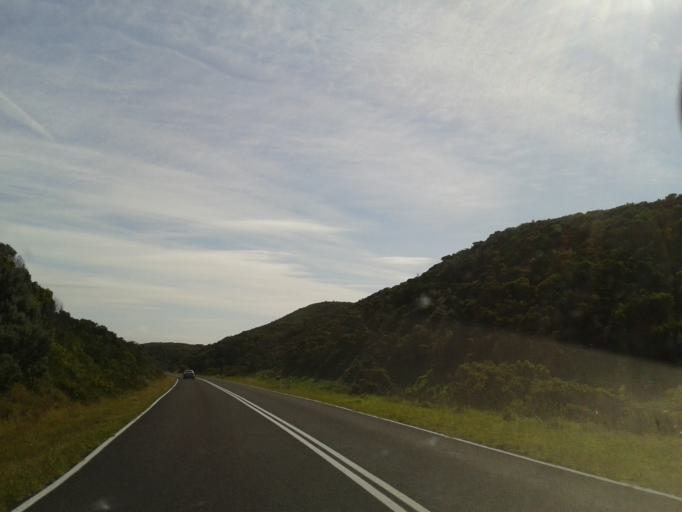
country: AU
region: Victoria
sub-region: Glenelg
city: Portland
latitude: -38.3600
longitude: 141.4286
